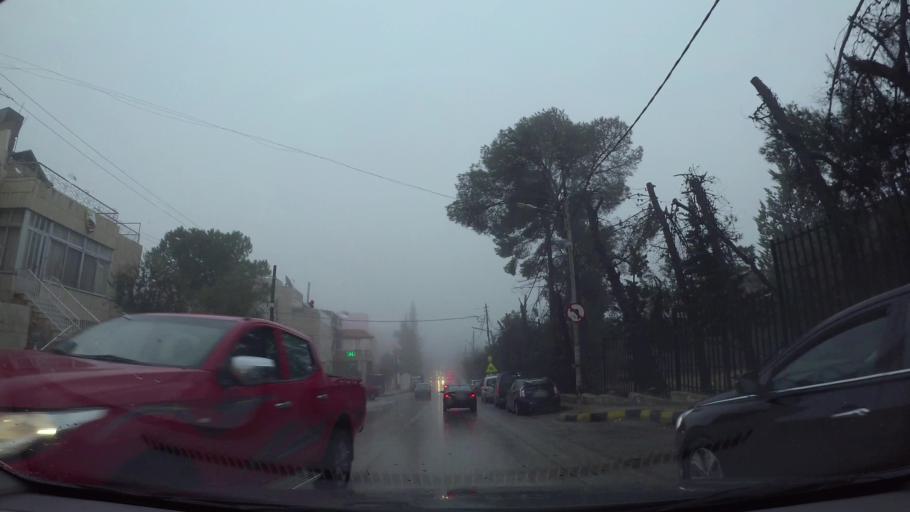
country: JO
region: Amman
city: Al Jubayhah
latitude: 32.0153
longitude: 35.8759
